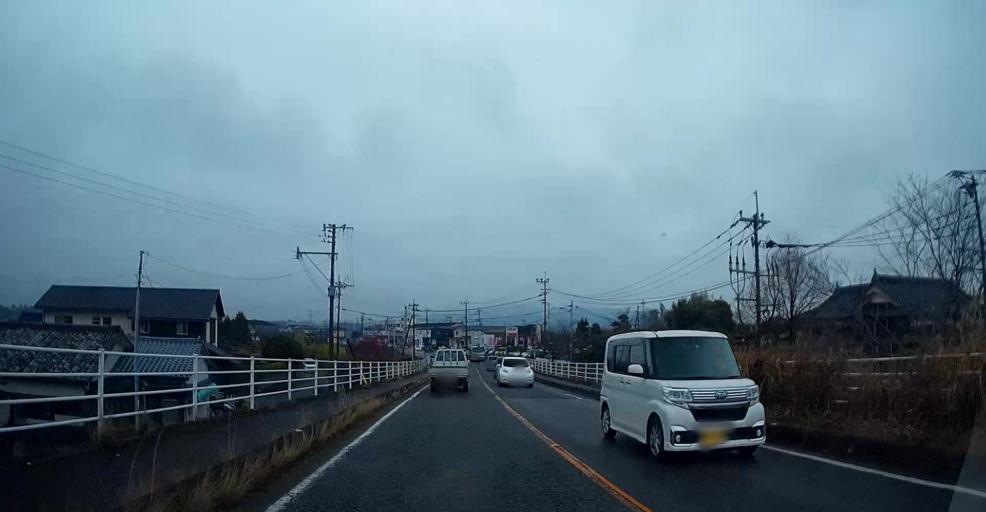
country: JP
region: Kumamoto
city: Uto
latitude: 32.7322
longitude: 130.7384
